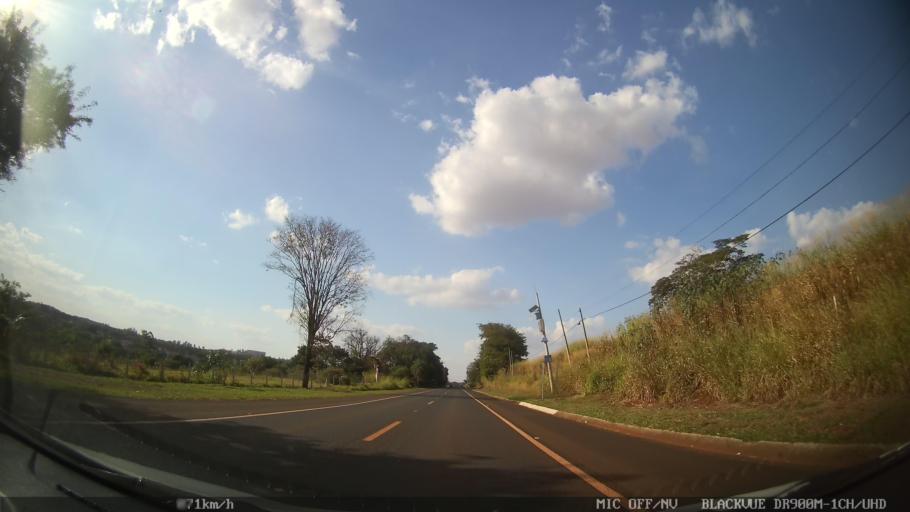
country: BR
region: Sao Paulo
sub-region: Ribeirao Preto
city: Ribeirao Preto
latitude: -21.1832
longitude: -47.8598
